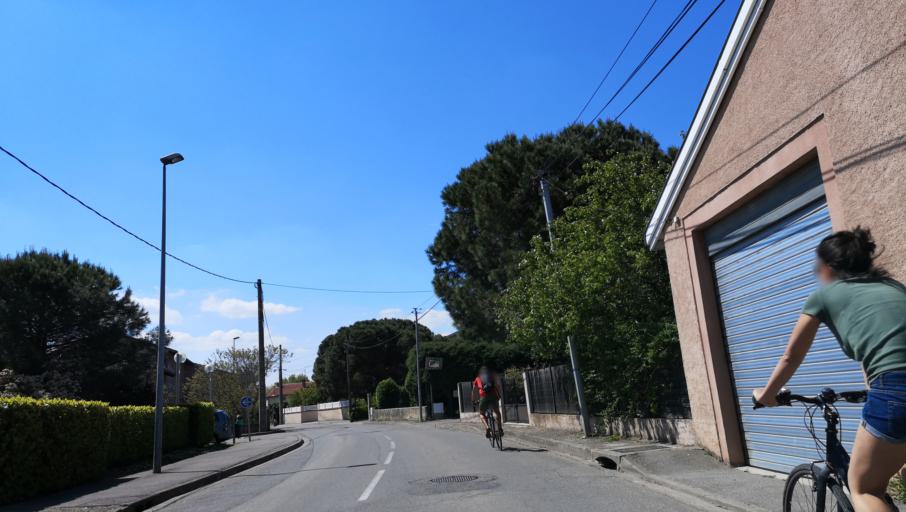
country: FR
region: Midi-Pyrenees
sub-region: Departement de la Haute-Garonne
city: Beauzelle
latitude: 43.6673
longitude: 1.3766
